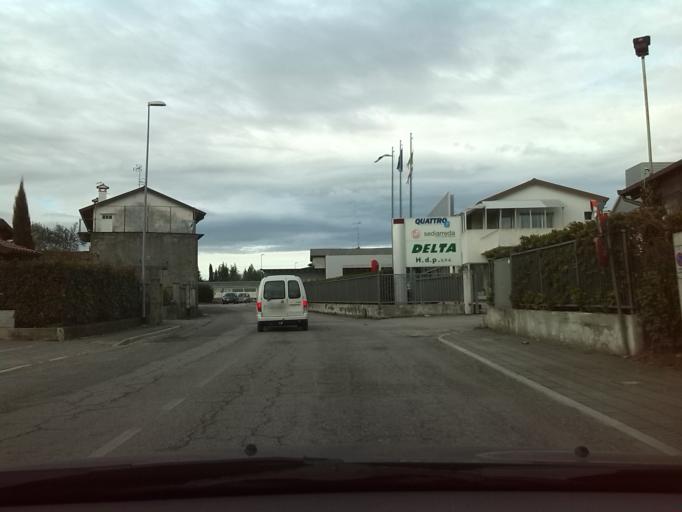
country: IT
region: Friuli Venezia Giulia
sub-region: Provincia di Udine
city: Manzano
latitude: 45.9943
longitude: 13.3916
